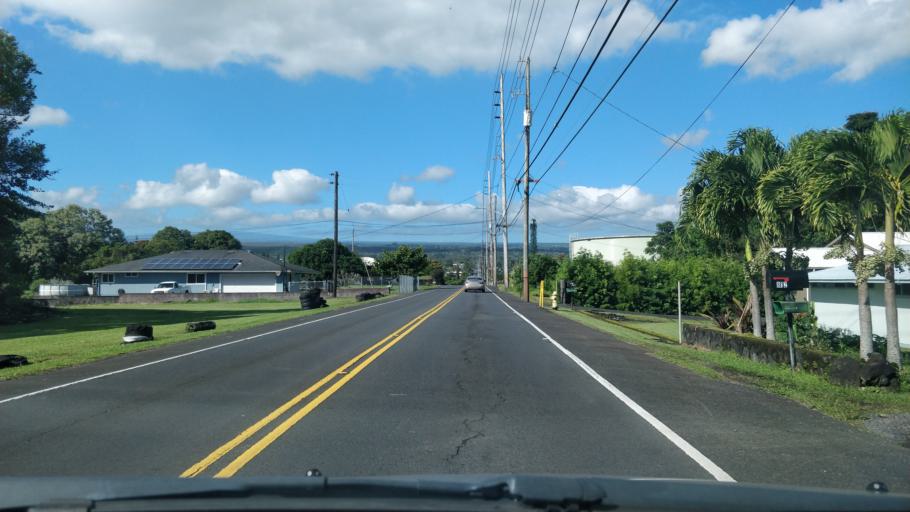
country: US
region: Hawaii
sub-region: Hawaii County
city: Hilo
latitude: 19.6831
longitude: -155.0909
